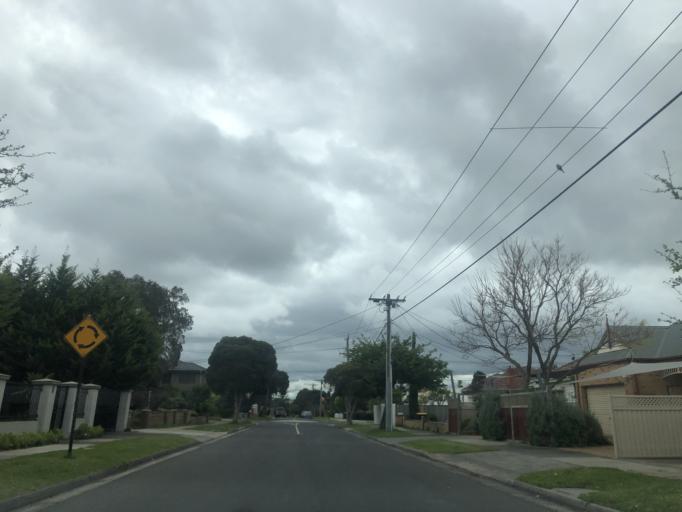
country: AU
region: Victoria
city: Clayton
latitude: -37.9243
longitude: 145.1098
